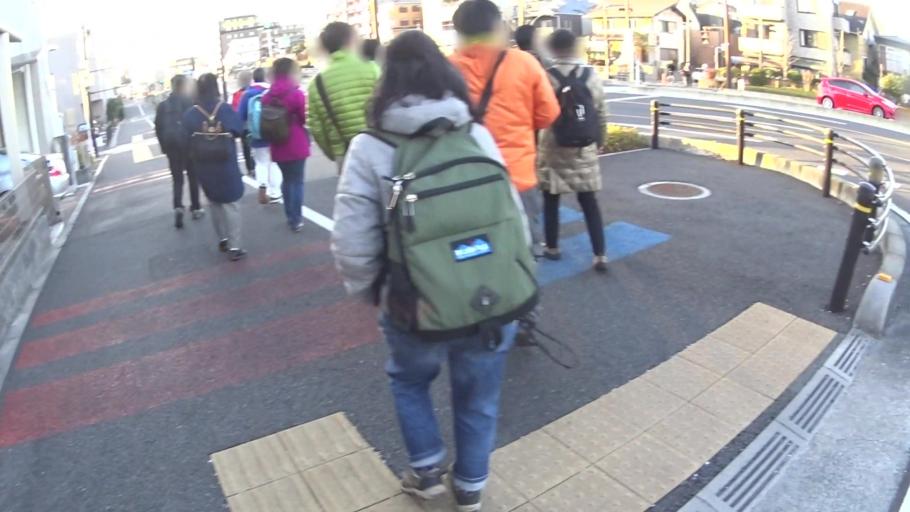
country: JP
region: Saitama
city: Yono
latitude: 35.8660
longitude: 139.6430
